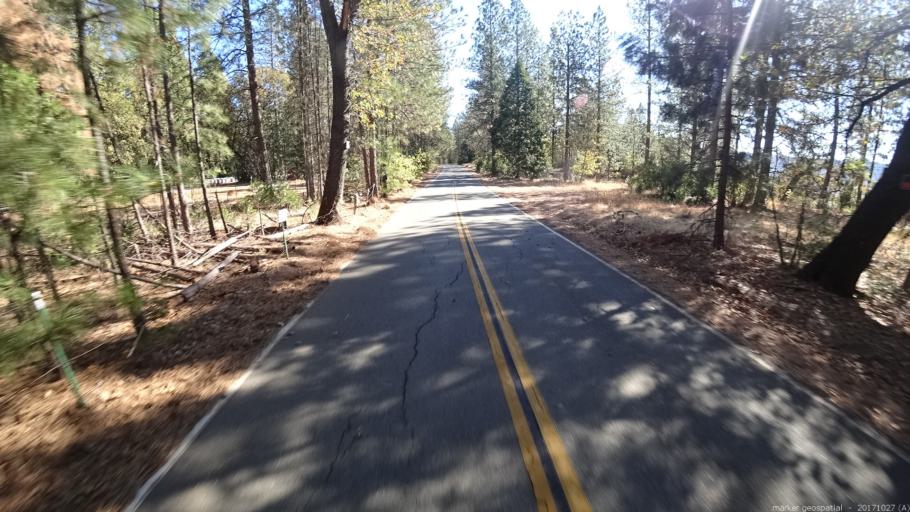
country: US
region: California
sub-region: Shasta County
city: Bella Vista
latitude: 40.7544
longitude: -121.9871
